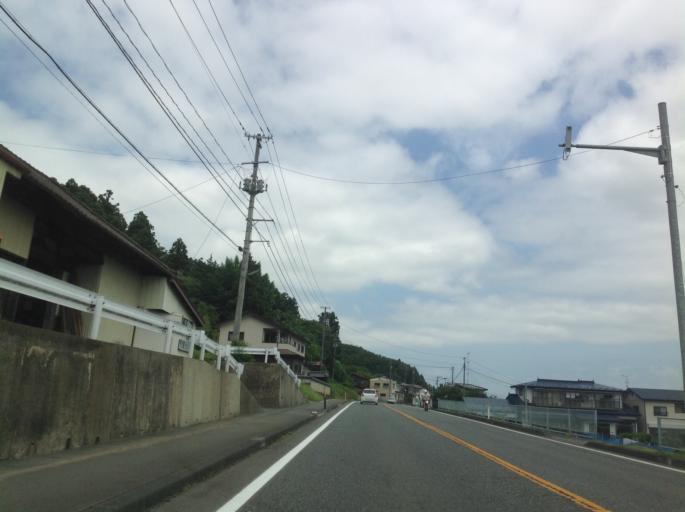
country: JP
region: Iwate
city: Mizusawa
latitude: 39.1115
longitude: 141.1429
